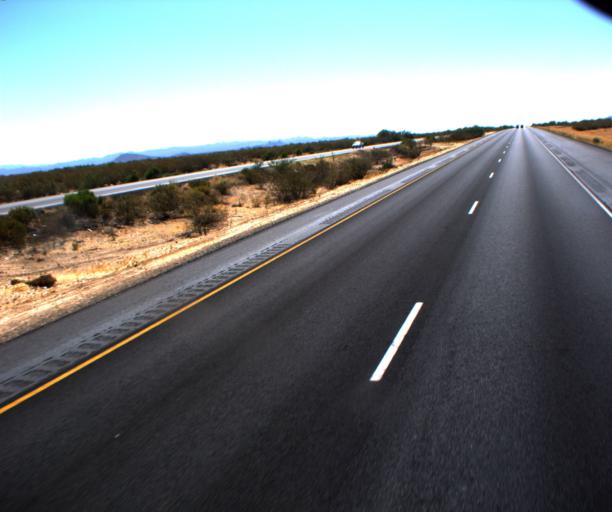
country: US
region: Arizona
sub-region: Yavapai County
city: Congress
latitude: 34.0728
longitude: -112.8784
